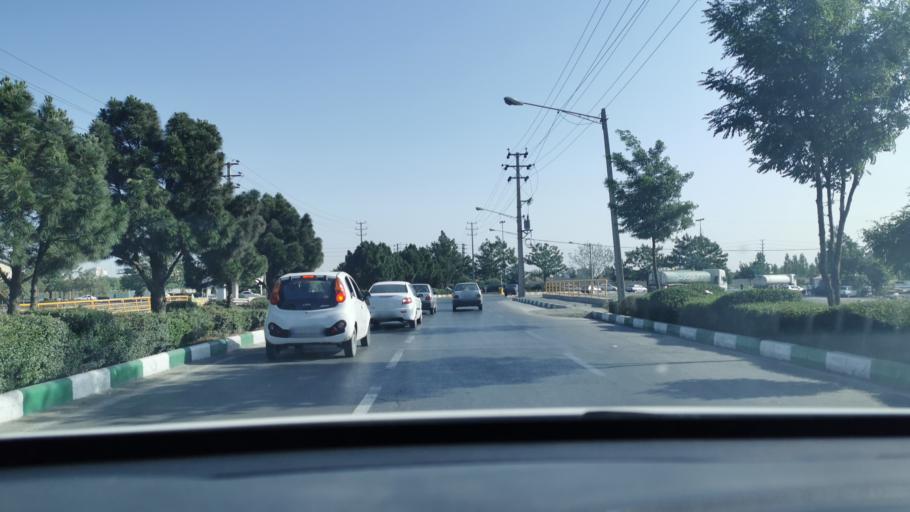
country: IR
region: Razavi Khorasan
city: Mashhad
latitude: 36.3440
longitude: 59.5081
